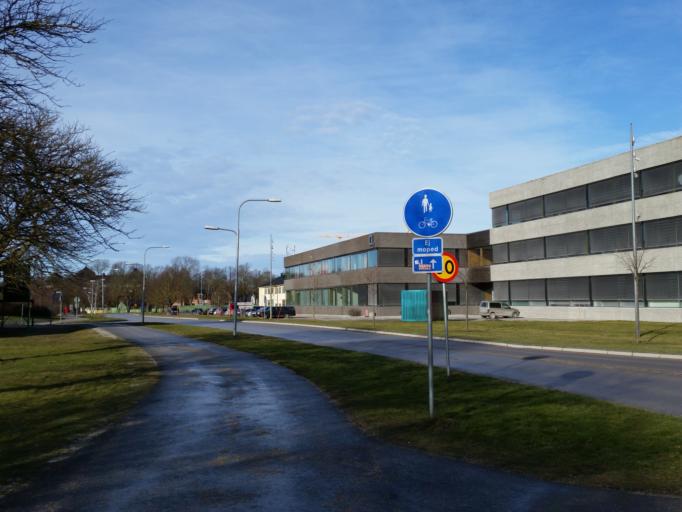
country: SE
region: Gotland
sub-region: Gotland
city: Visby
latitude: 57.6298
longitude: 18.3060
